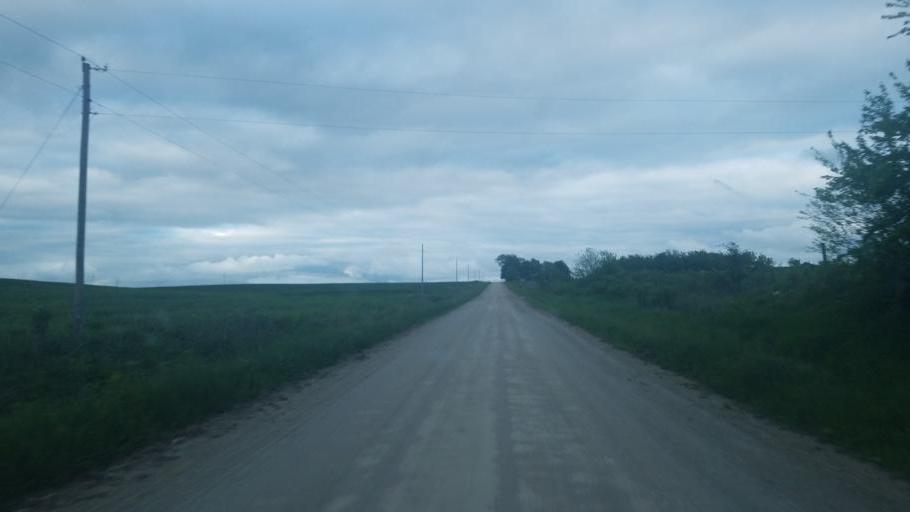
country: US
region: Iowa
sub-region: Decatur County
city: Lamoni
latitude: 40.5948
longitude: -93.9500
